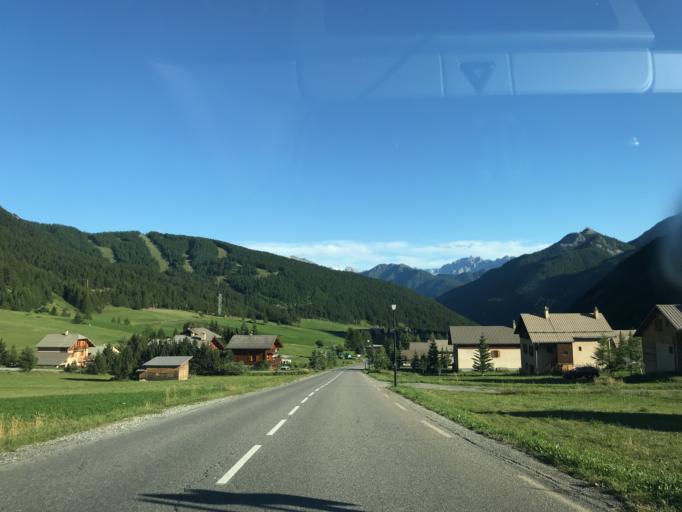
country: FR
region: Provence-Alpes-Cote d'Azur
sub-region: Departement des Hautes-Alpes
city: Villar-Saint-Pancrace
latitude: 44.7948
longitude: 6.7303
